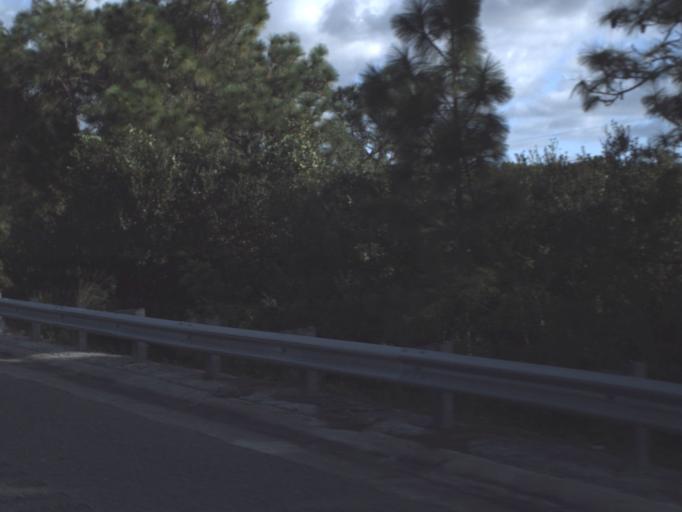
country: US
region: Florida
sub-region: Osceola County
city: Buenaventura Lakes
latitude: 28.3527
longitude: -81.3849
